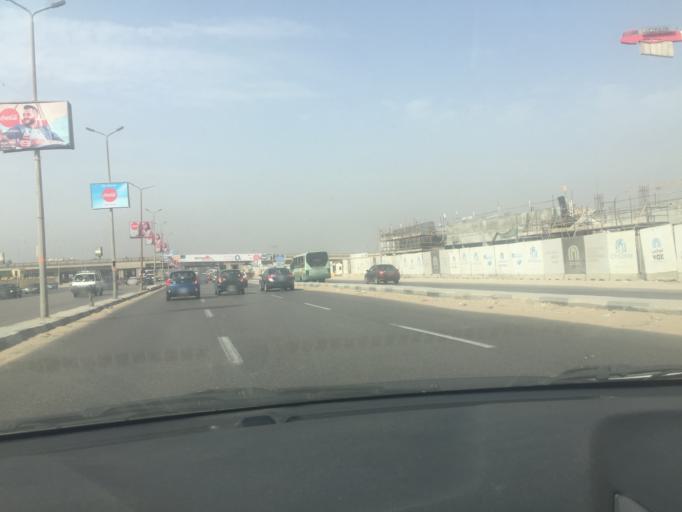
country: EG
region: Muhafazat al Qahirah
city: Cairo
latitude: 30.0798
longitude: 31.3649
